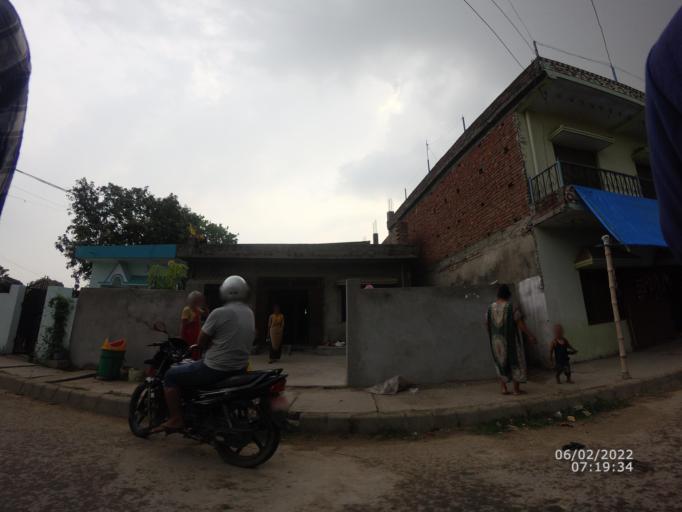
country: NP
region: Western Region
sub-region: Lumbini Zone
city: Bhairahawa
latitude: 27.4849
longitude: 83.4396
